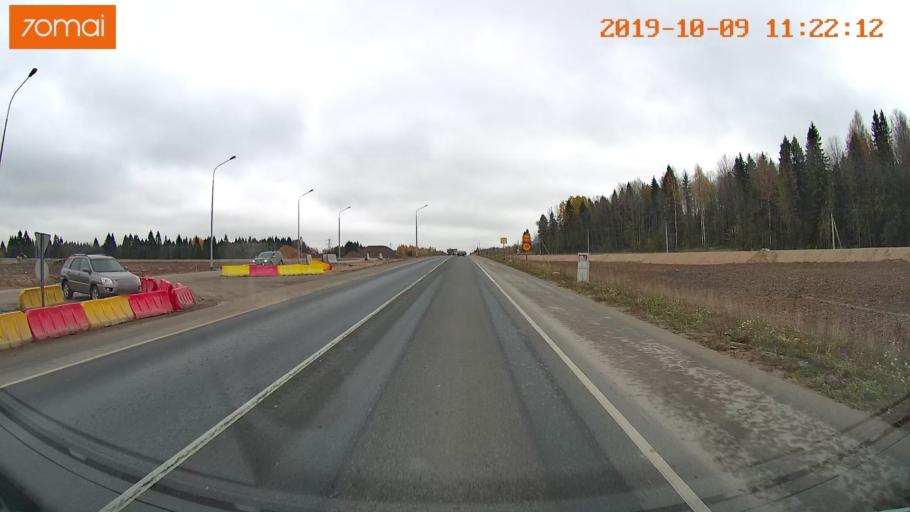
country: RU
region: Vologda
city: Vologda
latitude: 59.1337
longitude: 39.9558
